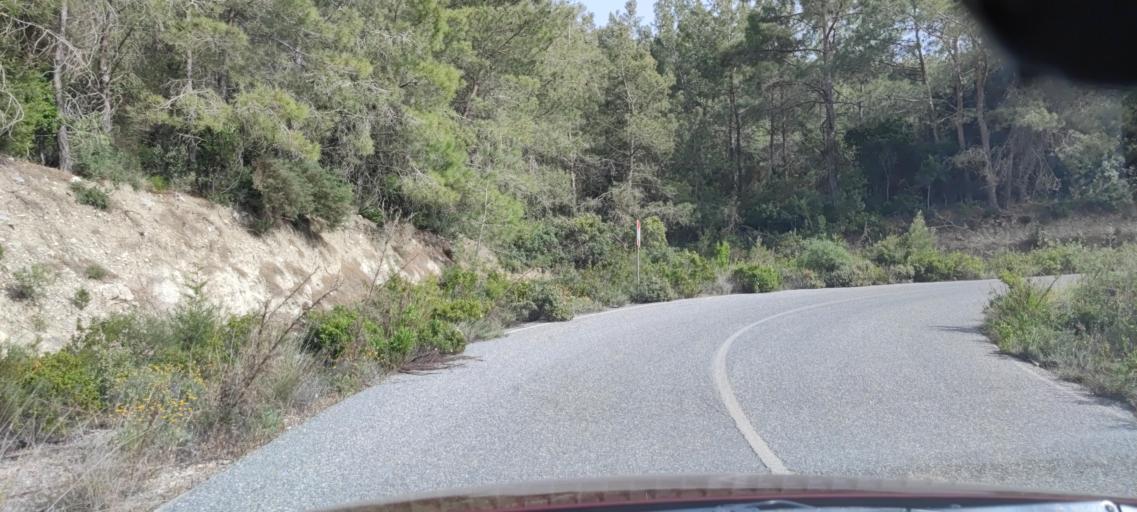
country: CY
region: Ammochostos
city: Trikomo
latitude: 35.3934
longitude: 33.8964
